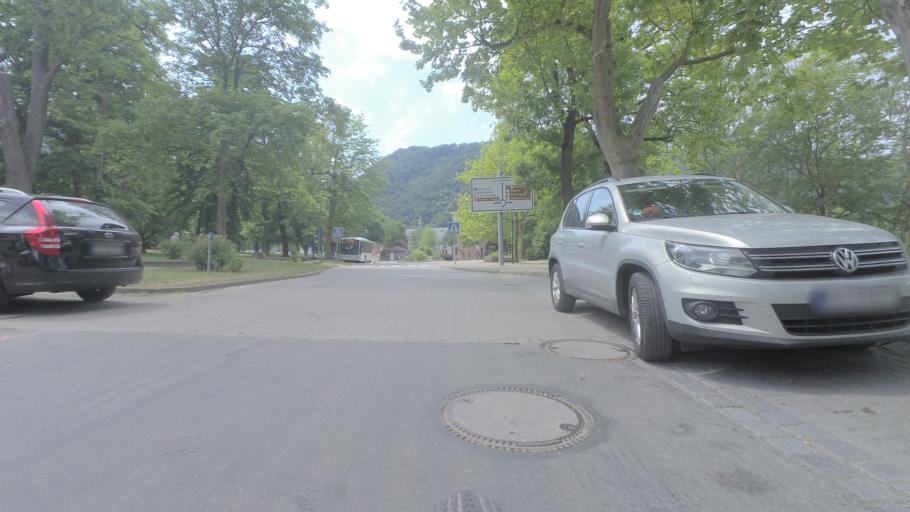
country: DE
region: Saxony-Anhalt
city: Thale
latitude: 51.7456
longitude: 11.0309
